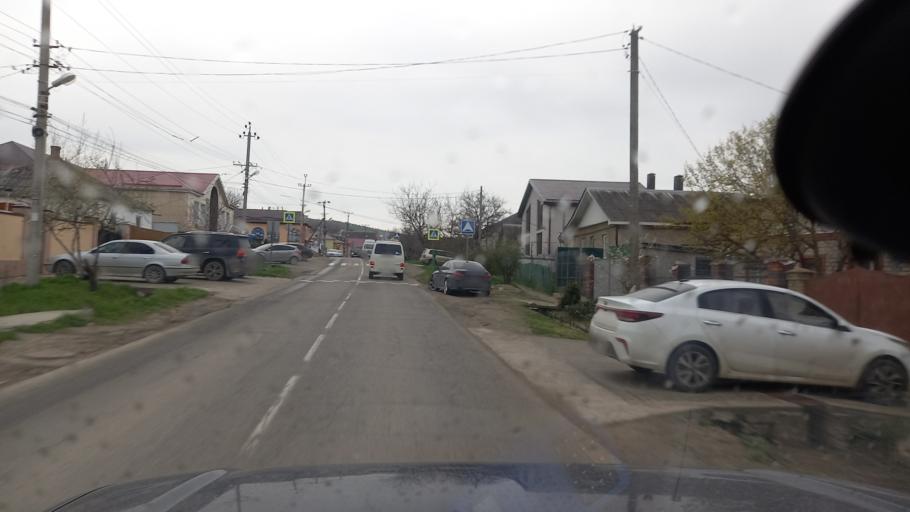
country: RU
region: Krasnodarskiy
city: Sukko
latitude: 44.8550
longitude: 37.4370
